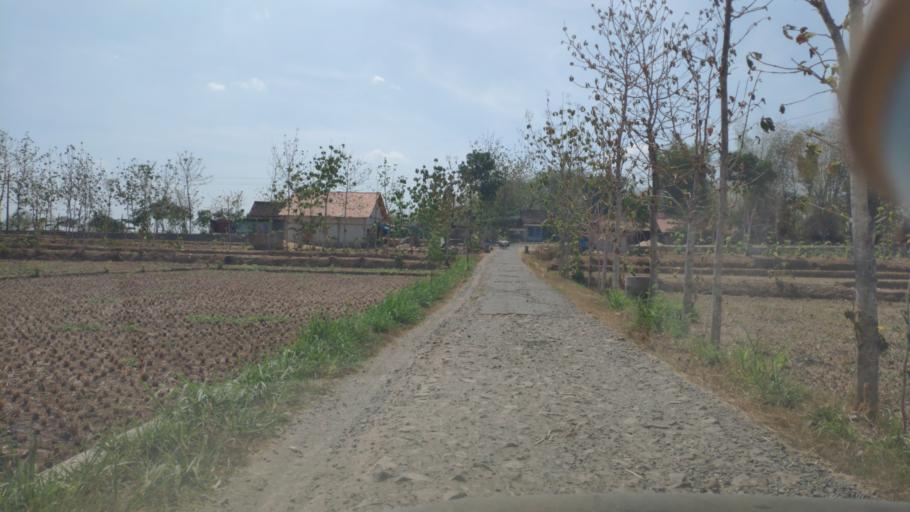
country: ID
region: Central Java
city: Sembungin
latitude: -6.9959
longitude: 111.3666
